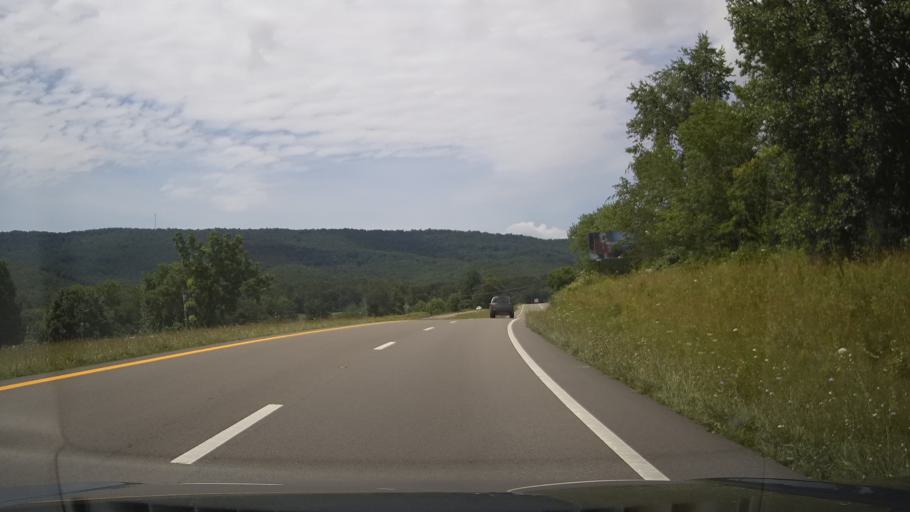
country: US
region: Virginia
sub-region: Lee County
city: Dryden
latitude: 36.7633
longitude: -82.8210
